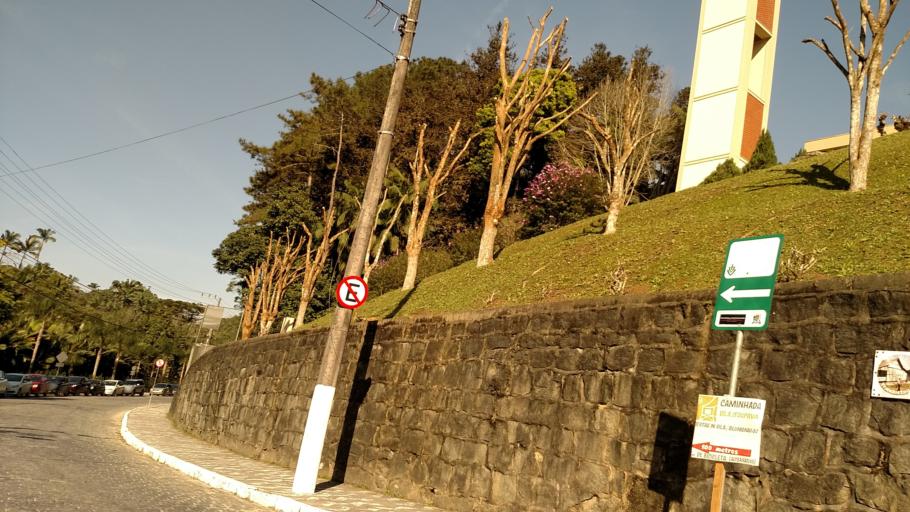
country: BR
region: Santa Catarina
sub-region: Pomerode
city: Pomerode
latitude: -26.7285
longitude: -49.0674
